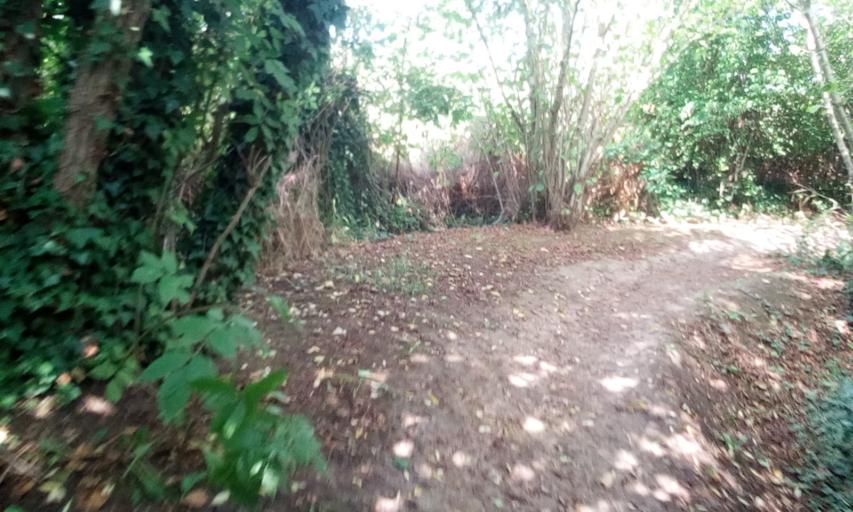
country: FR
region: Lower Normandy
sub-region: Departement du Calvados
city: Argences
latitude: 49.1262
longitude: -0.1463
